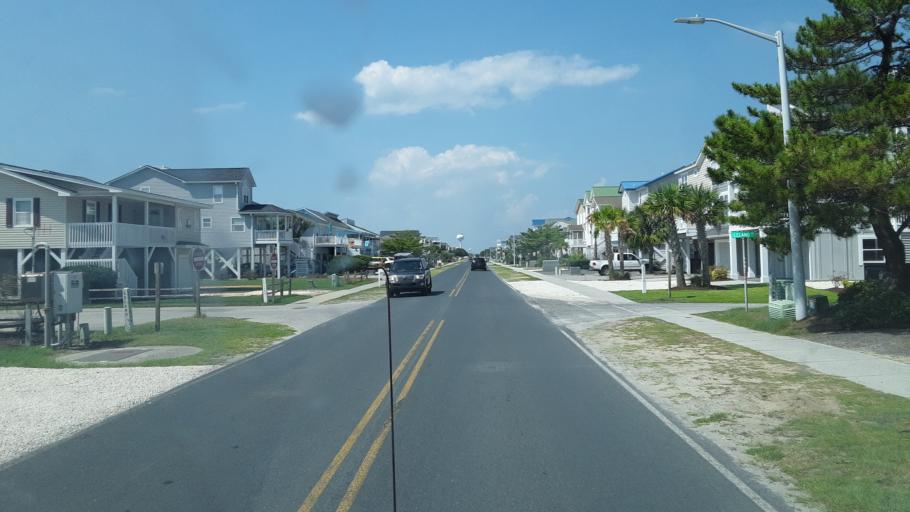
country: US
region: North Carolina
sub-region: Brunswick County
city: Shallotte
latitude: 33.8928
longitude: -78.4190
